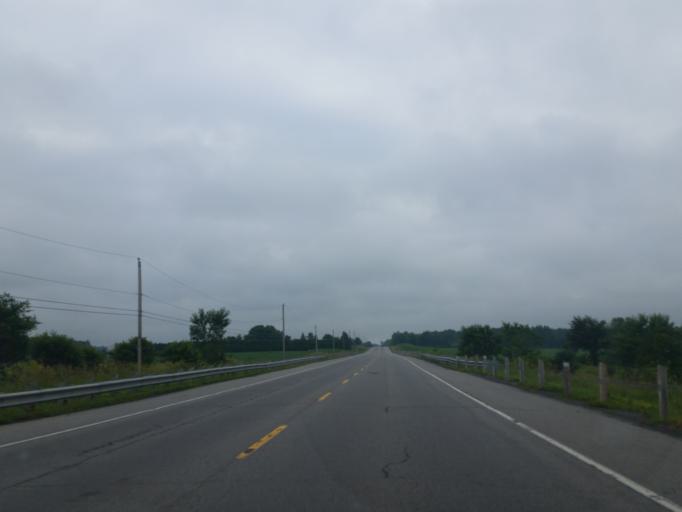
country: CA
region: Ontario
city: Clarence-Rockland
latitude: 45.3984
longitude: -75.3951
